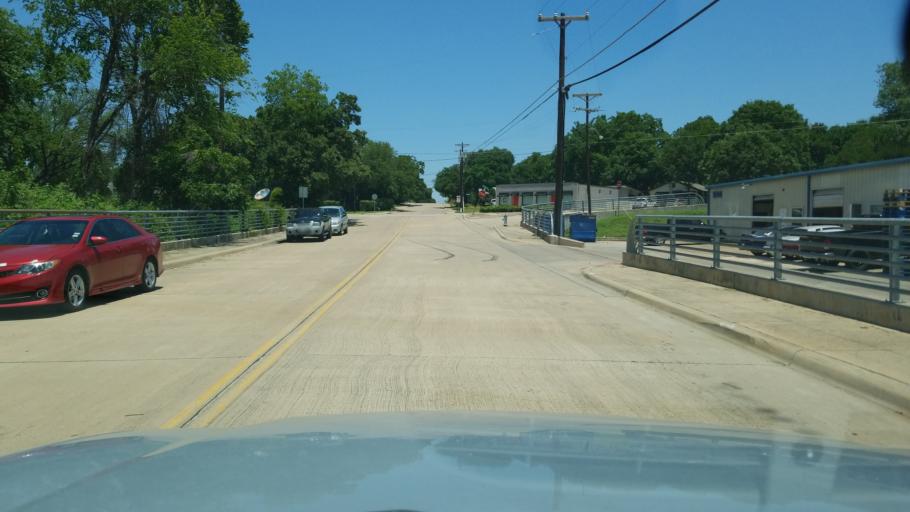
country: US
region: Texas
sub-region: Dallas County
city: Irving
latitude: 32.8029
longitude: -96.9170
